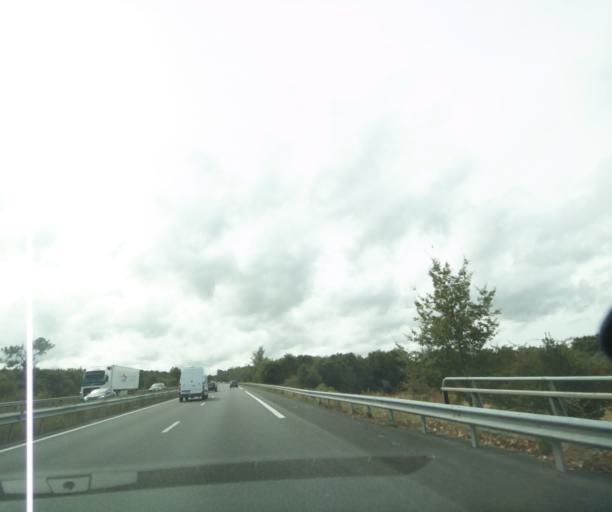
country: FR
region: Poitou-Charentes
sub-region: Departement de la Charente-Maritime
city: Saint-Genis-de-Saintonge
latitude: 45.4733
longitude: -0.6206
